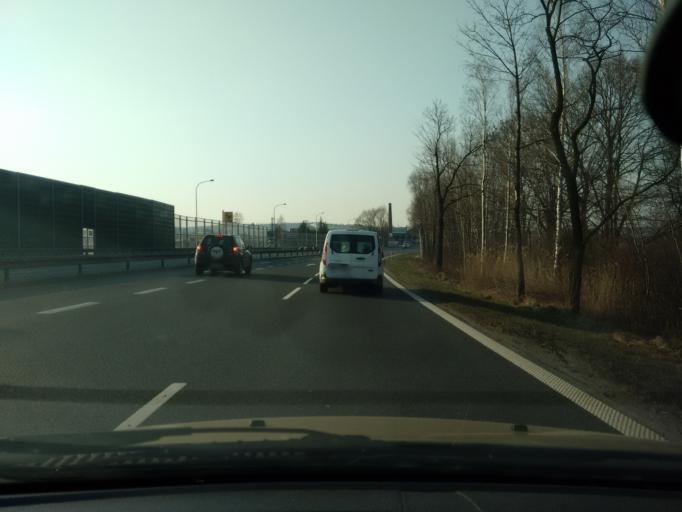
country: PL
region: Silesian Voivodeship
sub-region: Powiat cieszynski
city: Skoczow
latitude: 49.7914
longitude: 18.7987
